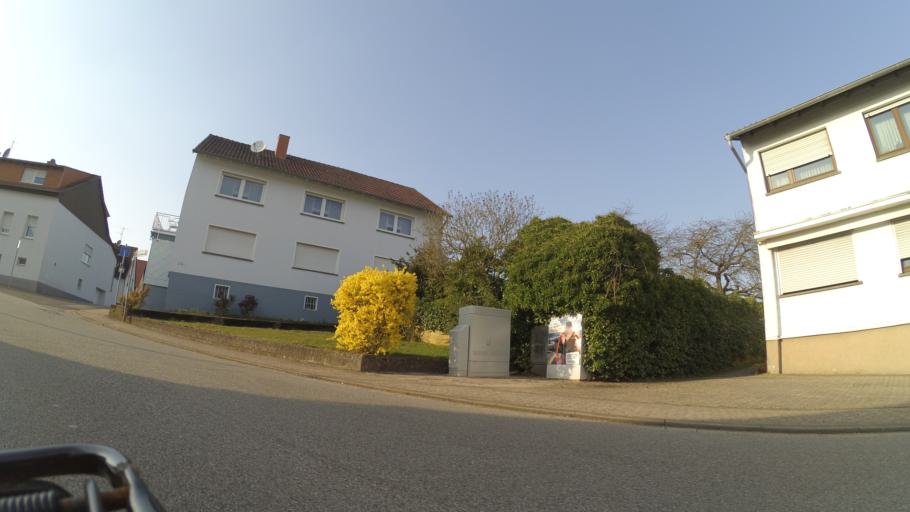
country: DE
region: Saarland
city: Heusweiler
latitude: 49.3486
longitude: 6.9825
